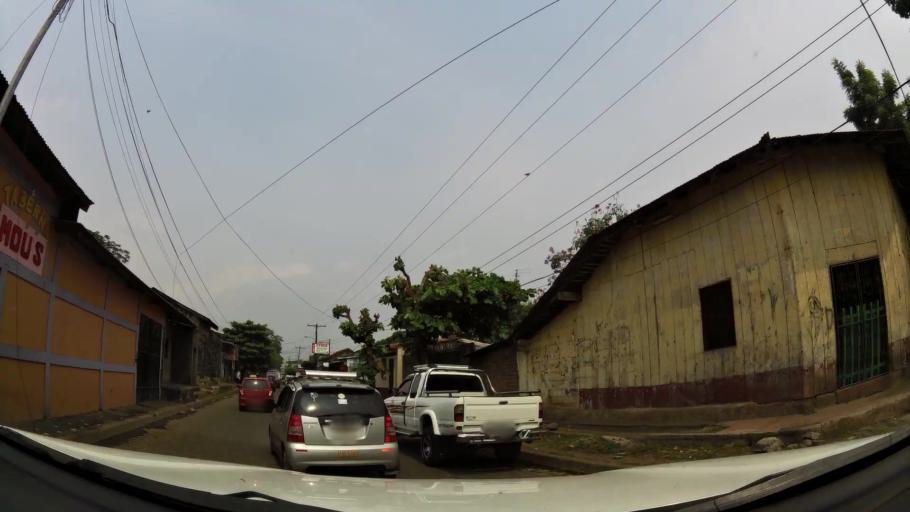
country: NI
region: Chinandega
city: Chinandega
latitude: 12.6238
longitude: -87.1316
